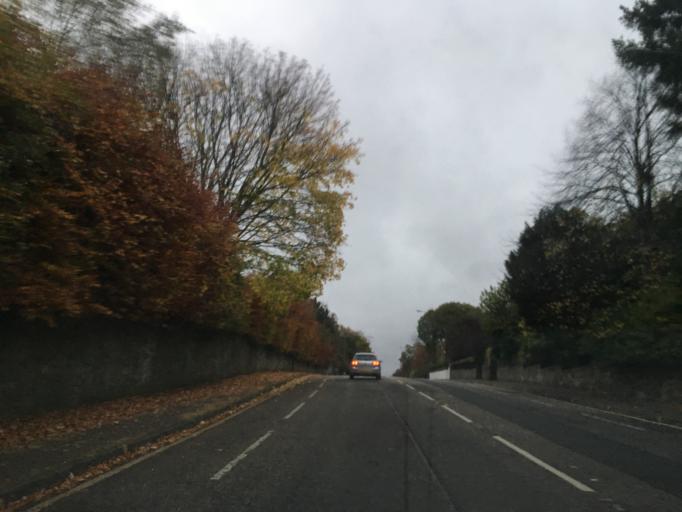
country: GB
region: Scotland
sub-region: Edinburgh
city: Edinburgh
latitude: 55.9212
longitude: -3.1686
